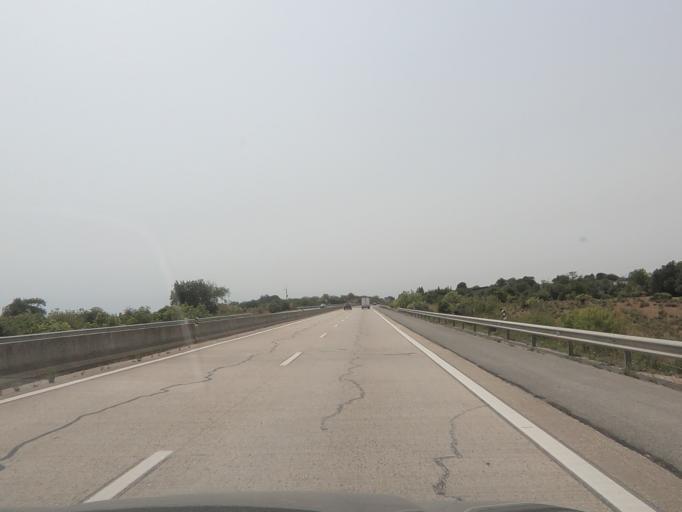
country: PT
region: Faro
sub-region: Albufeira
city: Guia
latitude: 37.1376
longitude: -8.2897
